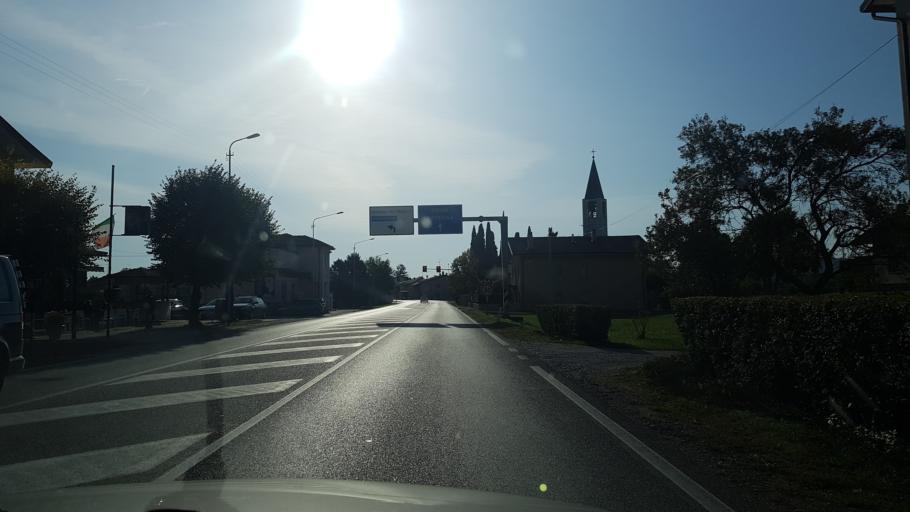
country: IT
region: Friuli Venezia Giulia
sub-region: Provincia di Udine
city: Gemona
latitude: 46.2536
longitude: 13.1143
